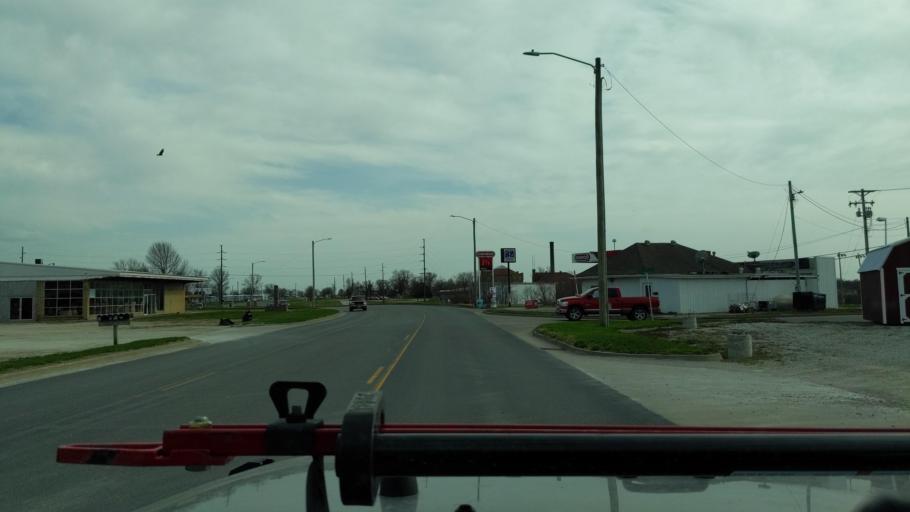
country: US
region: Missouri
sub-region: Macon County
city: Macon
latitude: 39.7253
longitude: -92.4662
